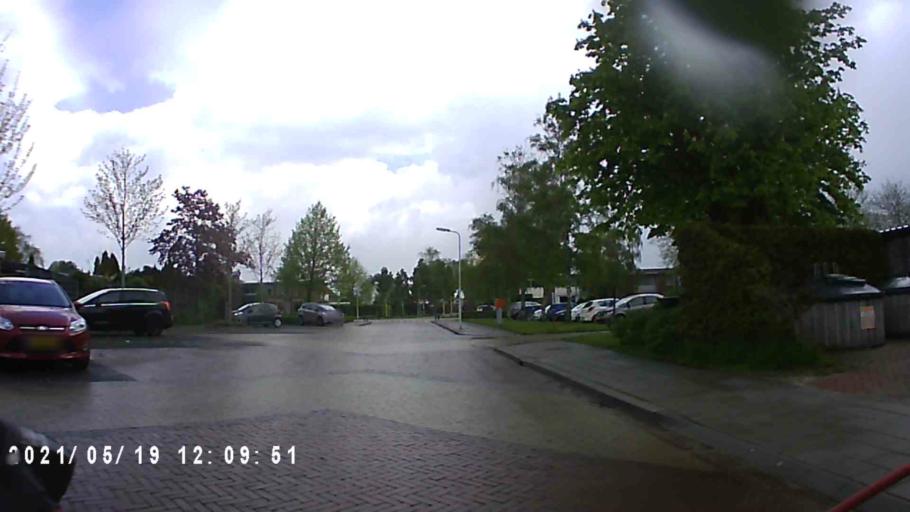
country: NL
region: Friesland
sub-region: Gemeente Achtkarspelen
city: Buitenpost
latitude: 53.2502
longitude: 6.1414
